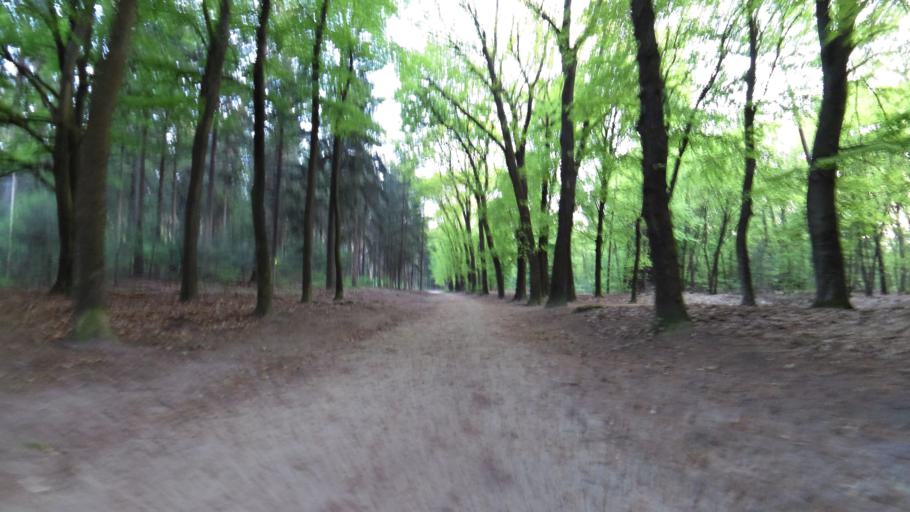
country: NL
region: Gelderland
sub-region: Gemeente Ede
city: Ede
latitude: 52.0302
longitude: 5.6908
